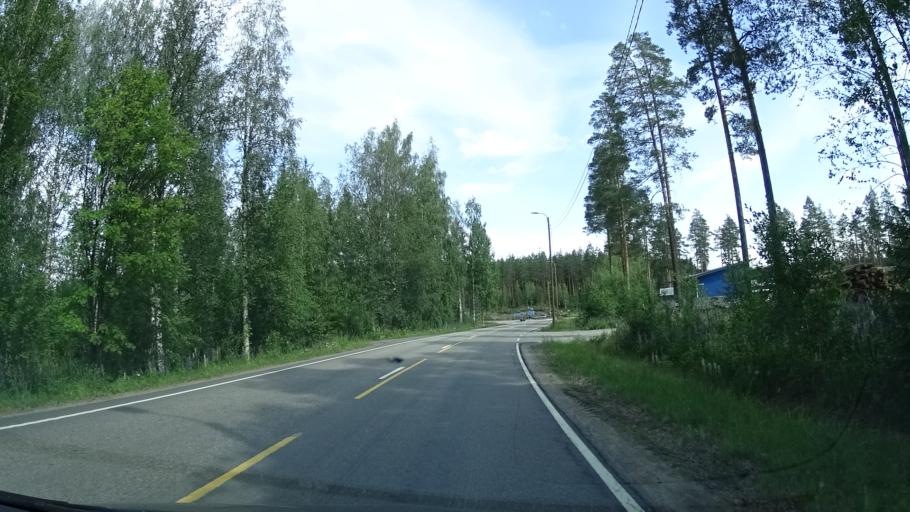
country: FI
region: Central Finland
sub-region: Keuruu
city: Multia
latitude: 62.4155
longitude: 24.8206
